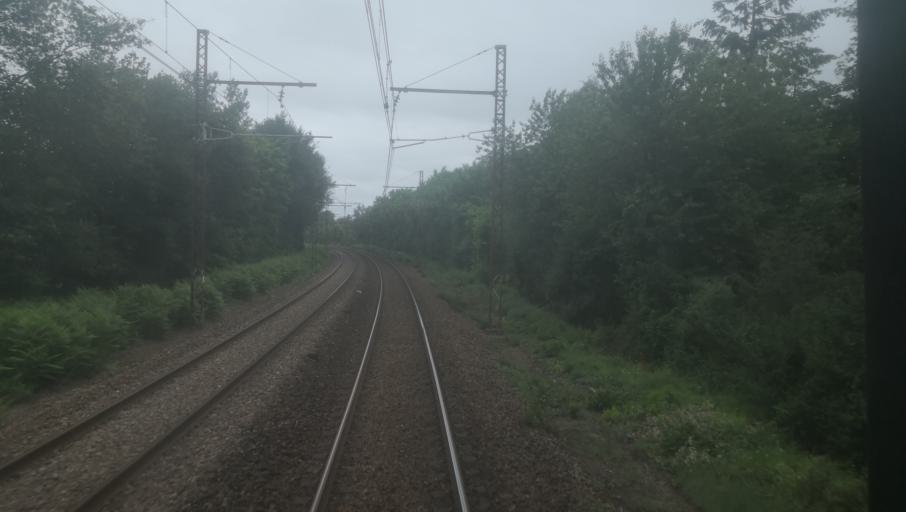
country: FR
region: Centre
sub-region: Departement de l'Indre
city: Chantome
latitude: 46.4533
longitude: 1.5502
